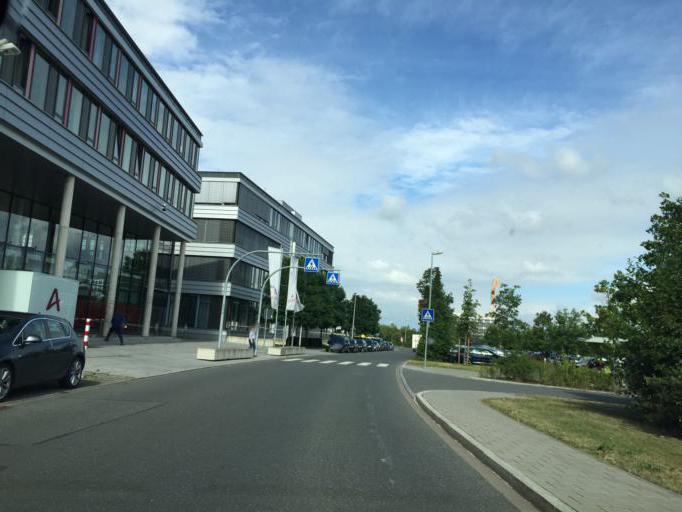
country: DE
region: Bavaria
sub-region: Regierungsbezirk Mittelfranken
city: Erlangen
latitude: 49.5710
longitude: 11.0066
